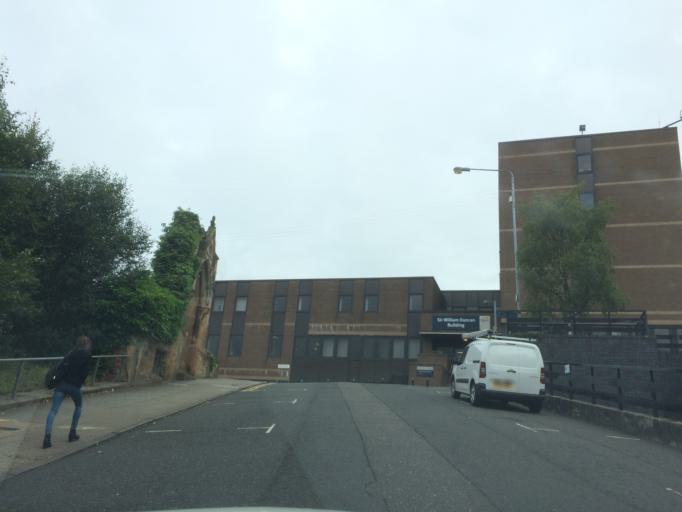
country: GB
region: Scotland
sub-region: Glasgow City
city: Glasgow
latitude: 55.8619
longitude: -4.2432
